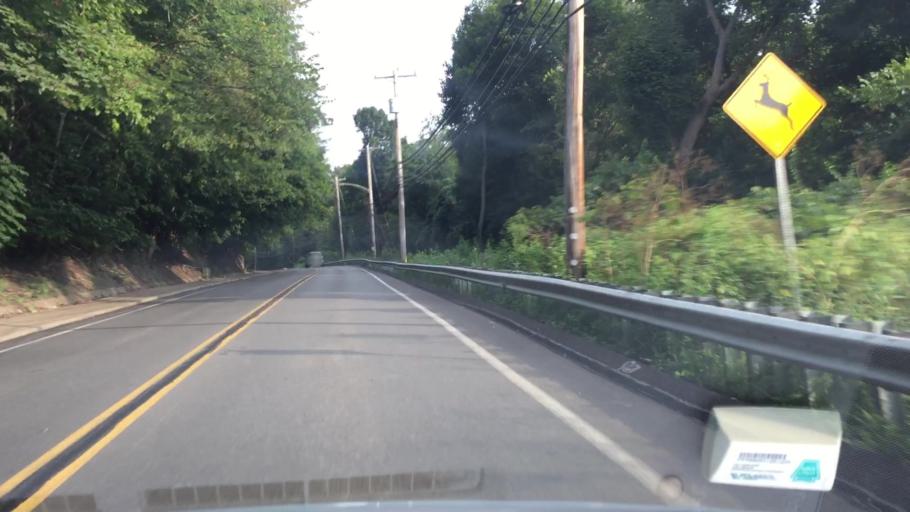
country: US
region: Pennsylvania
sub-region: Allegheny County
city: McKees Rocks
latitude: 40.4767
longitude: -80.0740
